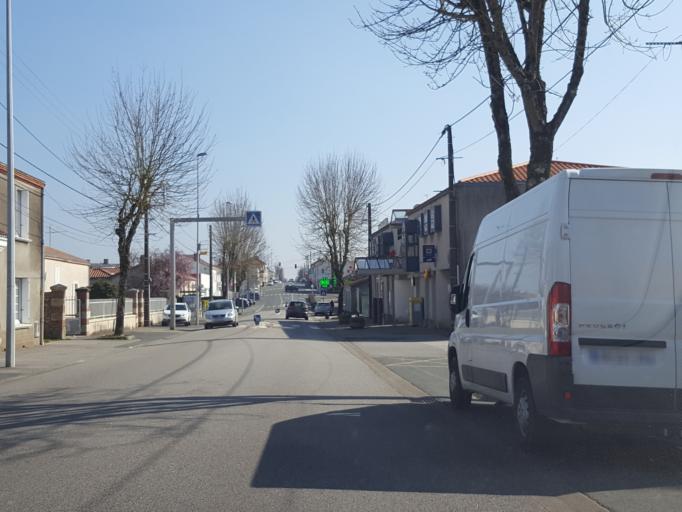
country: FR
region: Pays de la Loire
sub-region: Departement de la Vendee
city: La Roche-sur-Yon
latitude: 46.6609
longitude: -1.4053
